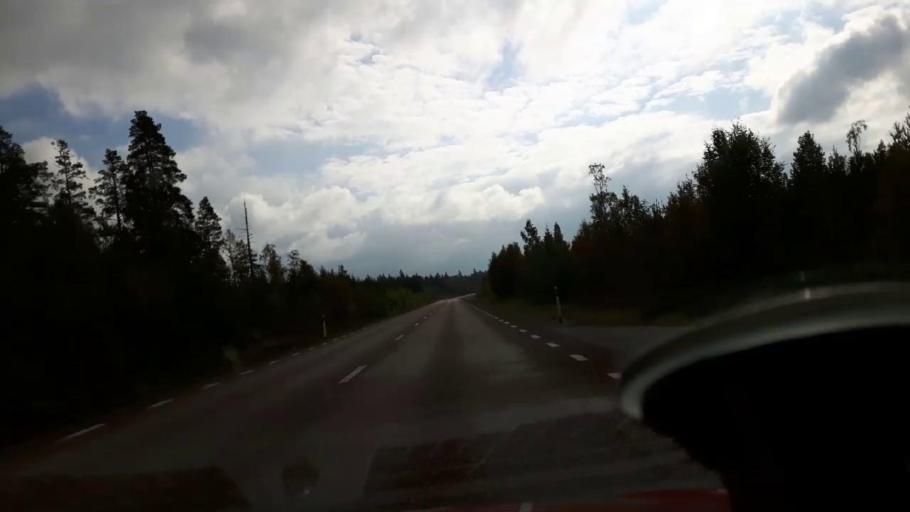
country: SE
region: Gaevleborg
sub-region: Soderhamns Kommun
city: Ljusne
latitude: 61.0848
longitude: 16.9591
